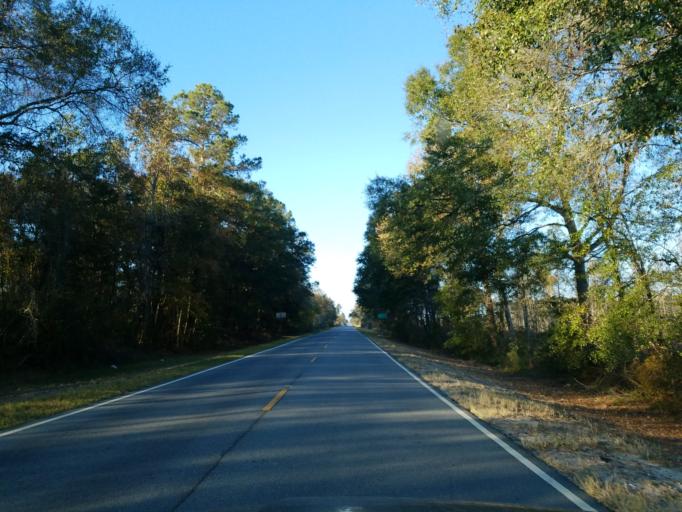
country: US
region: Georgia
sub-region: Lanier County
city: Lakeland
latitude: 31.1409
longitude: -83.0864
